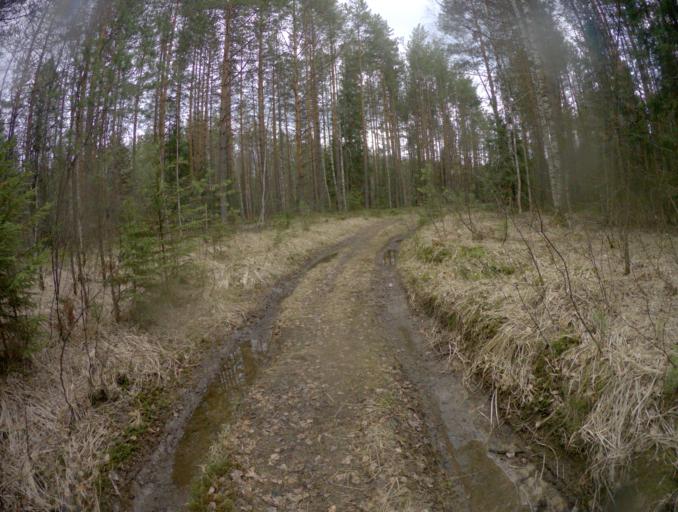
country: RU
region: Vladimir
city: Raduzhnyy
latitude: 55.9501
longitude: 40.2704
